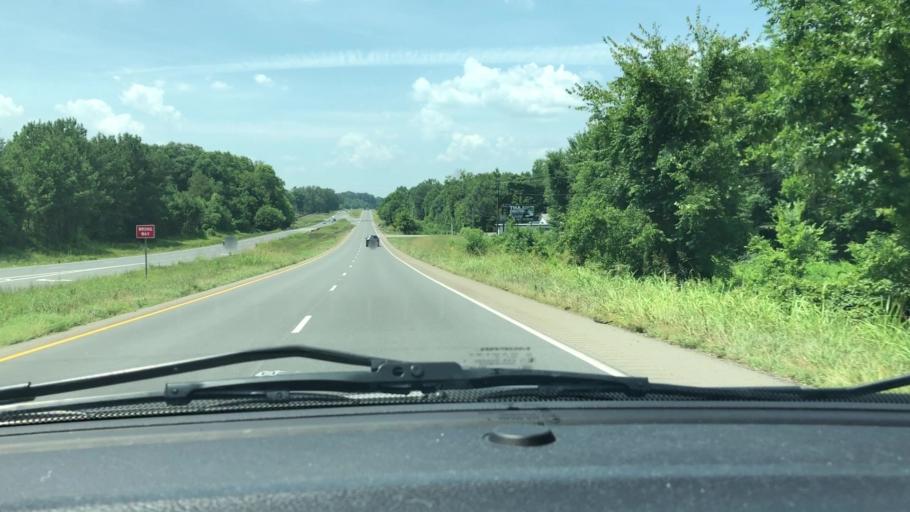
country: US
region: North Carolina
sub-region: Chatham County
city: Siler City
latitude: 35.6580
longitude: -79.3983
